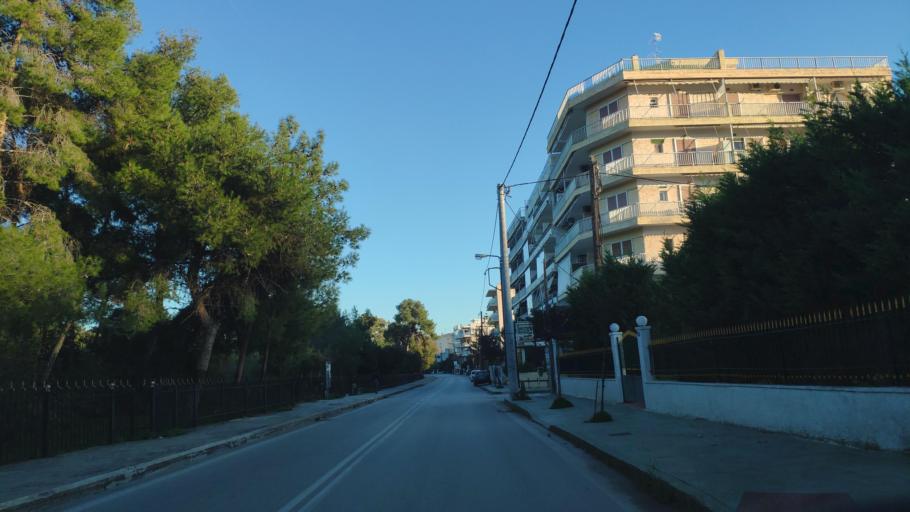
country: GR
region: Peloponnese
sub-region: Nomos Korinthias
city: Xylokastro
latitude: 38.0742
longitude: 22.6412
